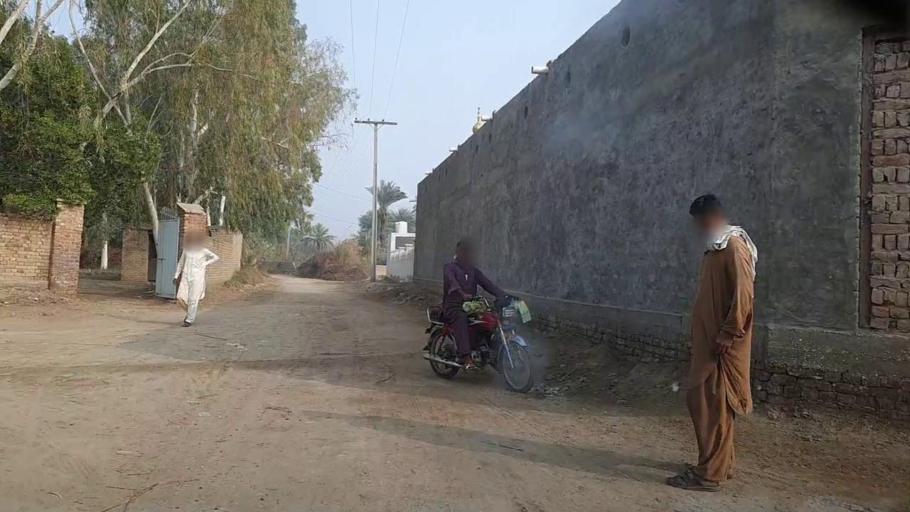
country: PK
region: Sindh
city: Bozdar
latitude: 27.1447
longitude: 68.6493
